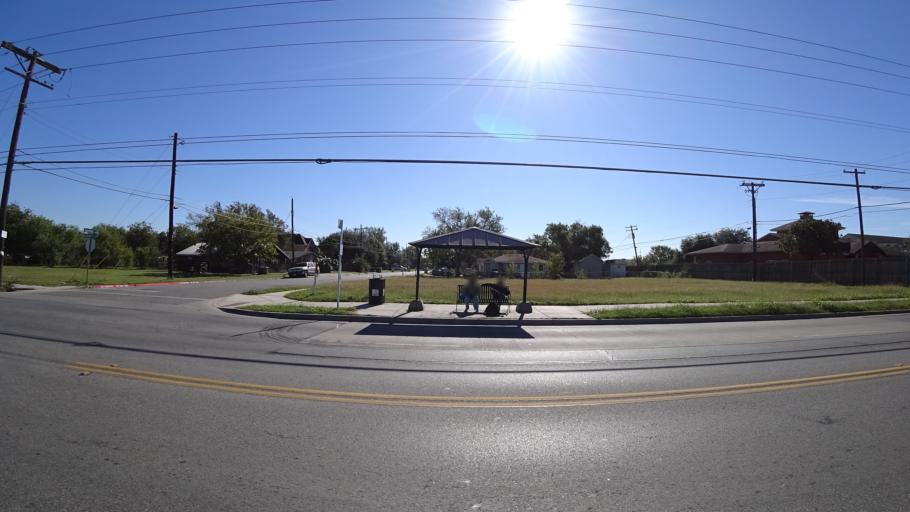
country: US
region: Texas
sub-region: Travis County
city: Austin
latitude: 30.2288
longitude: -97.7011
